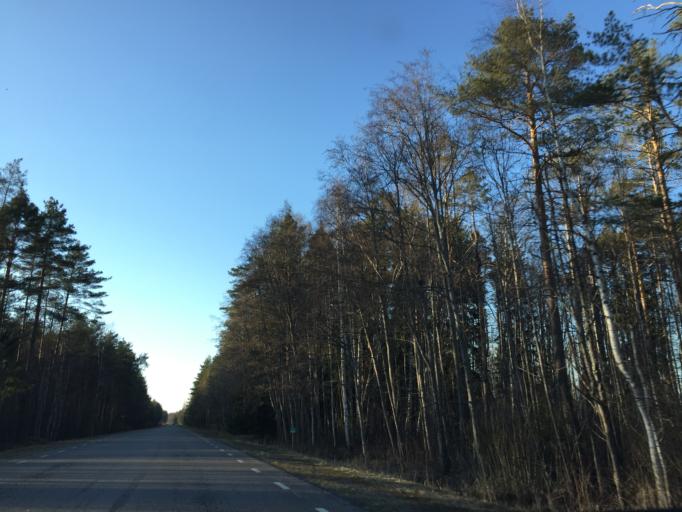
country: EE
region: Ida-Virumaa
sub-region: Toila vald
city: Voka
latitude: 59.1004
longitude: 27.6498
